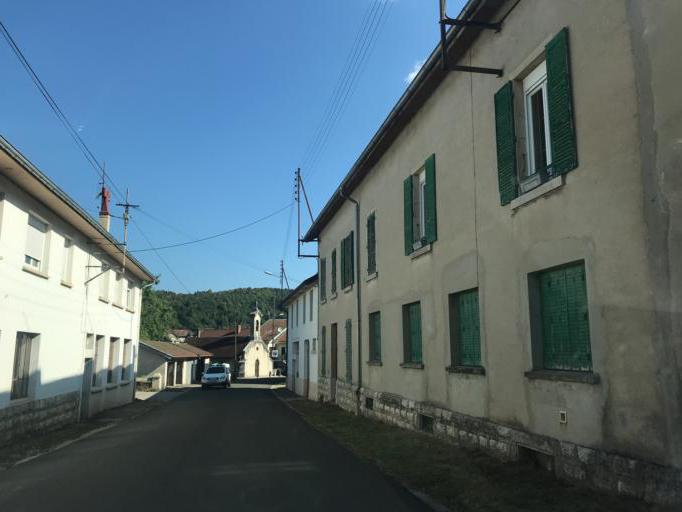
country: FR
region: Franche-Comte
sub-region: Departement du Jura
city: Moirans-en-Montagne
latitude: 46.4127
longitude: 5.7349
